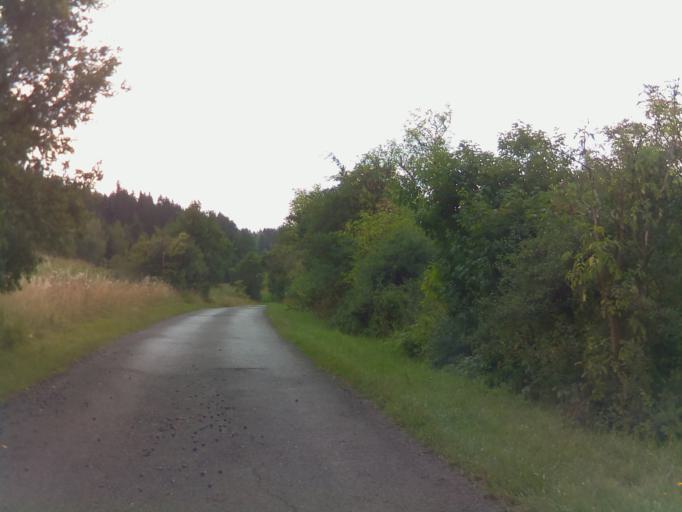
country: DE
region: Thuringia
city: Veilsdorf
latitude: 50.3993
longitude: 10.7892
